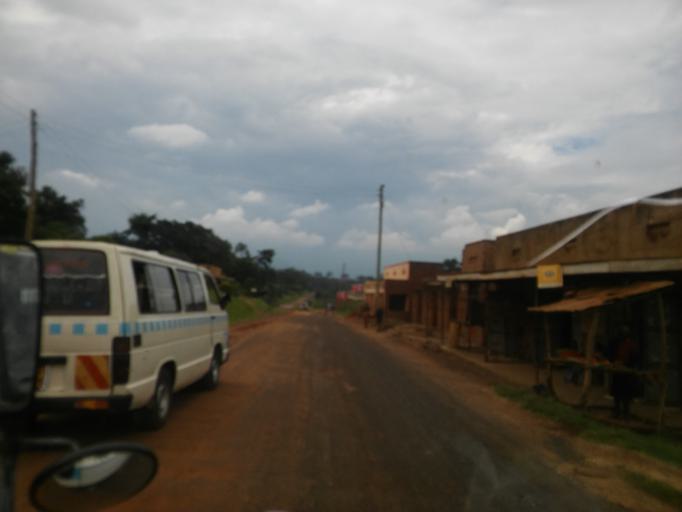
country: UG
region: Eastern Region
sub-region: Bududa District
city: Bududa
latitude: 0.9498
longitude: 34.2583
